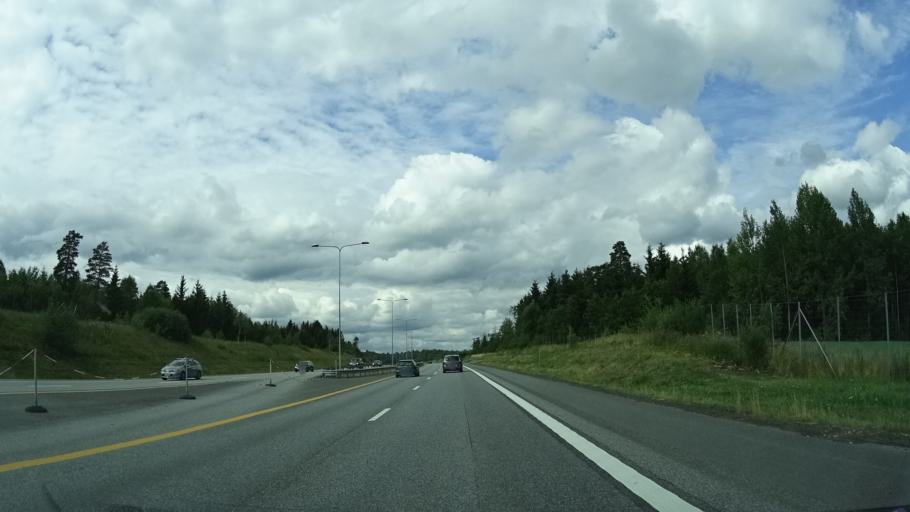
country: NO
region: Vestfold
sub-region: Holmestrand
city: Holmestrand
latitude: 59.4720
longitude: 10.2904
